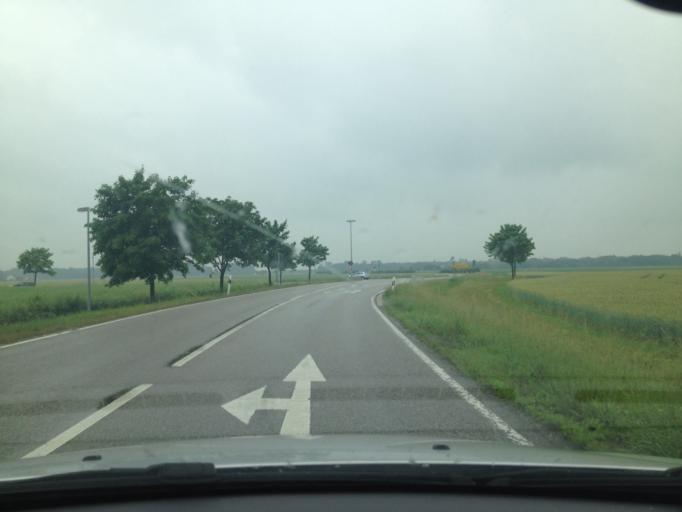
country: DE
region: Bavaria
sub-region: Swabia
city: Klosterlechfeld
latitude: 48.1729
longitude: 10.8293
